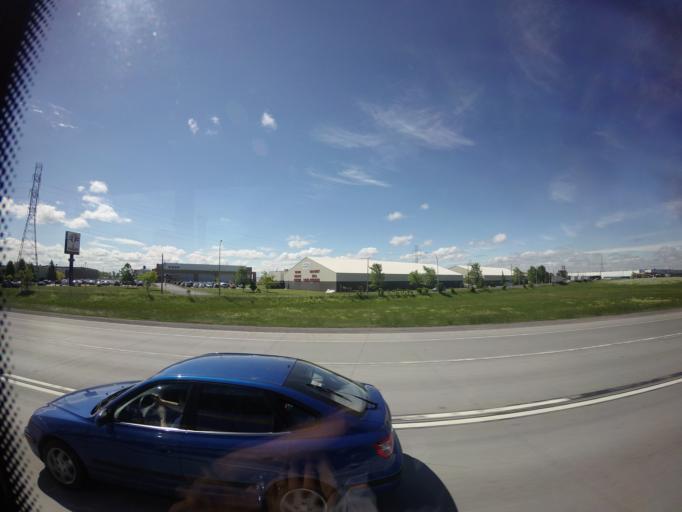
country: CA
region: Quebec
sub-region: Monteregie
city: Boucherville
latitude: 45.5699
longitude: -73.4033
